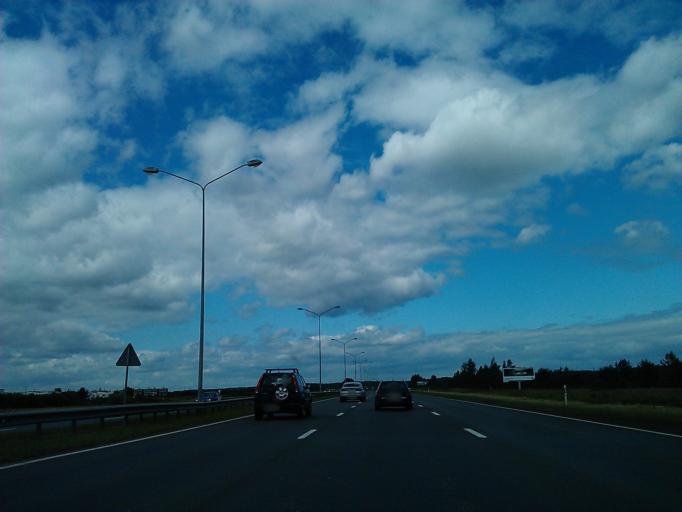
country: LV
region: Babite
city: Pinki
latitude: 56.9569
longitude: 23.9099
